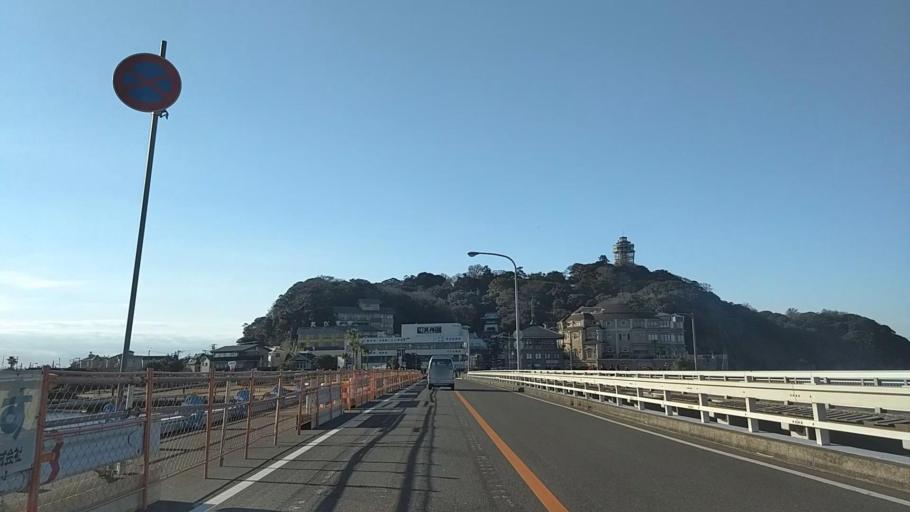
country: JP
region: Kanagawa
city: Fujisawa
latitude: 35.3040
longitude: 139.4821
